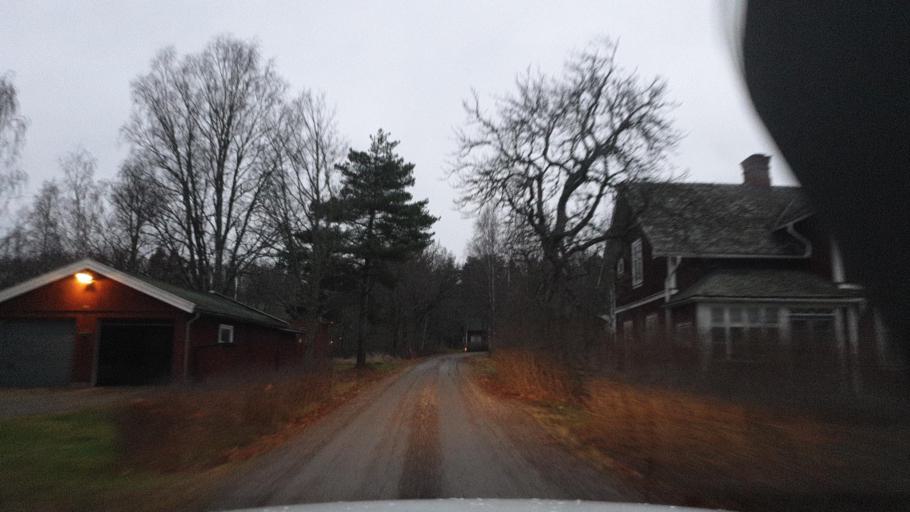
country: SE
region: Vaermland
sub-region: Eda Kommun
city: Amotfors
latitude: 59.7924
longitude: 12.4434
